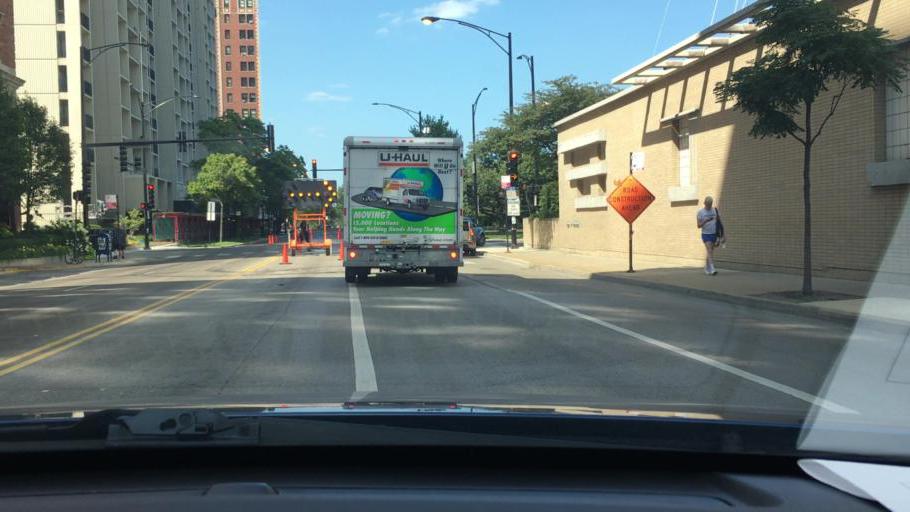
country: US
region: Illinois
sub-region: Cook County
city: Chicago
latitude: 41.9396
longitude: -87.6395
